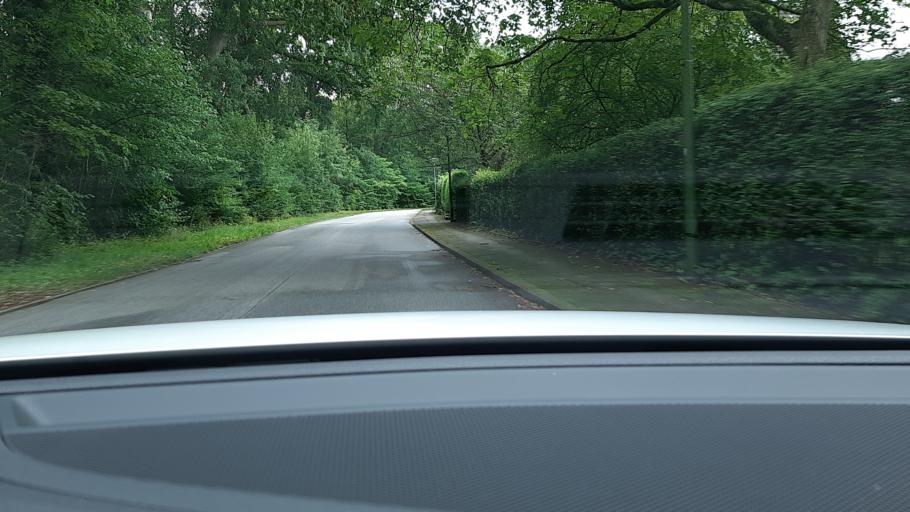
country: DE
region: Schleswig-Holstein
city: Bad Schwartau
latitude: 53.8940
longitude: 10.7314
